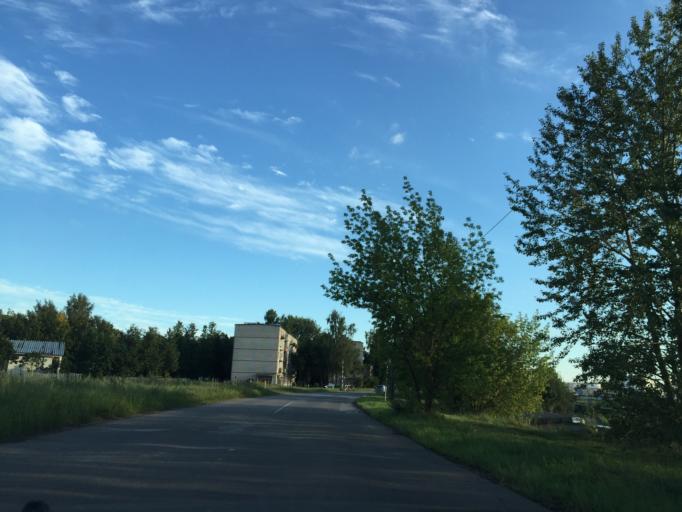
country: LV
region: Riga
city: Jaunciems
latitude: 57.0105
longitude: 24.1244
